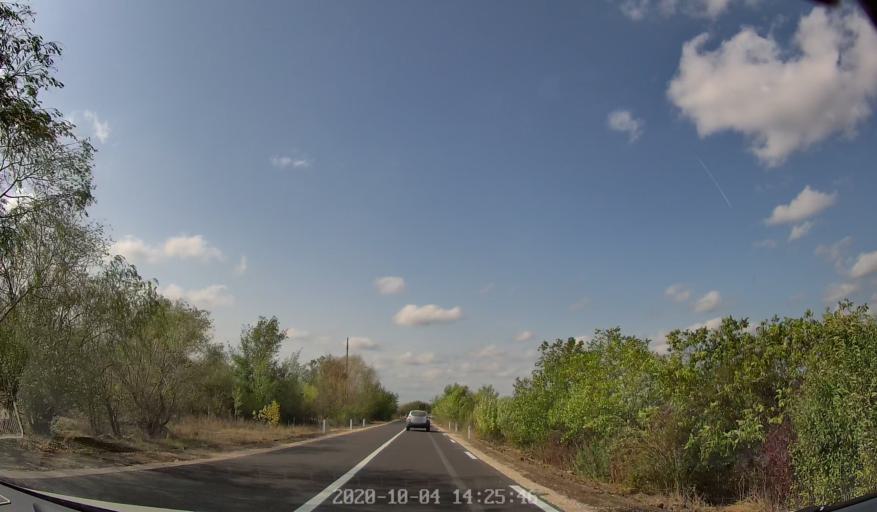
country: MD
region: Rezina
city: Saharna
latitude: 47.6224
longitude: 28.8940
